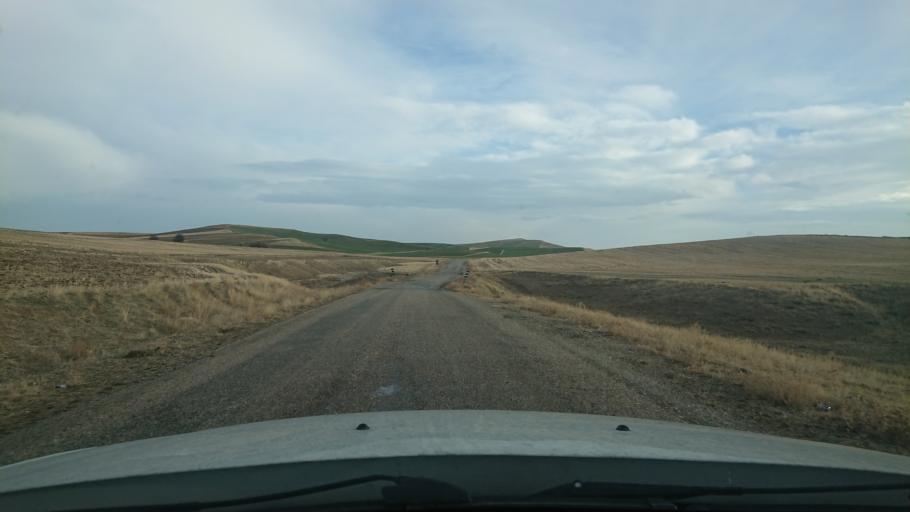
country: TR
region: Aksaray
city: Acipinar
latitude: 38.6431
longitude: 33.8090
